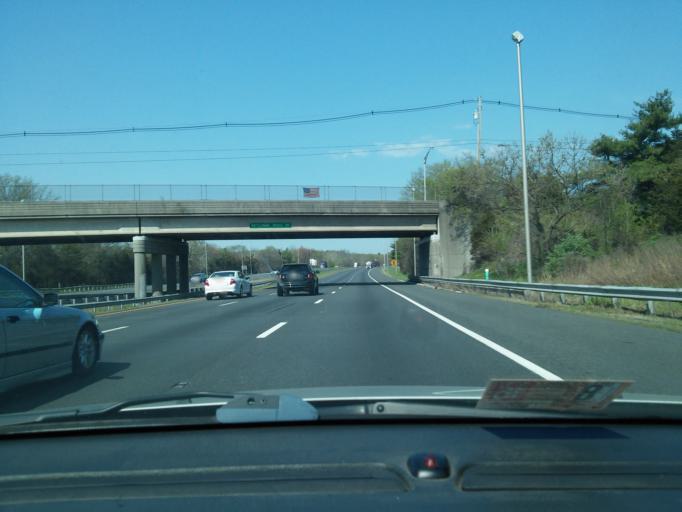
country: US
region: New Jersey
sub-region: Hunterdon County
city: Whitehouse Station
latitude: 40.6445
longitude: -74.7156
